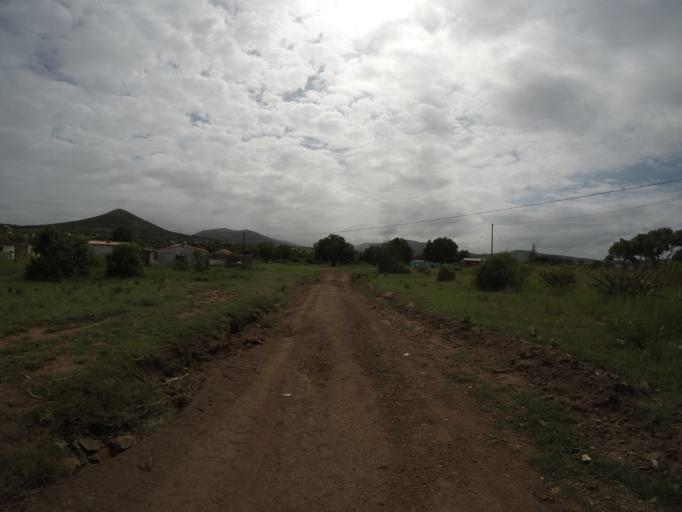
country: ZA
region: KwaZulu-Natal
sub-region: uThungulu District Municipality
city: Empangeni
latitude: -28.6150
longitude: 31.8503
